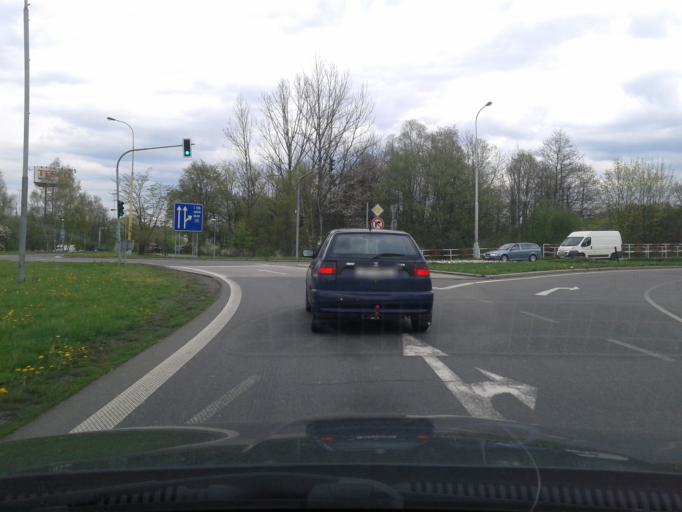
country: CZ
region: Moravskoslezsky
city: Havirov
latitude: 49.7889
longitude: 18.4136
